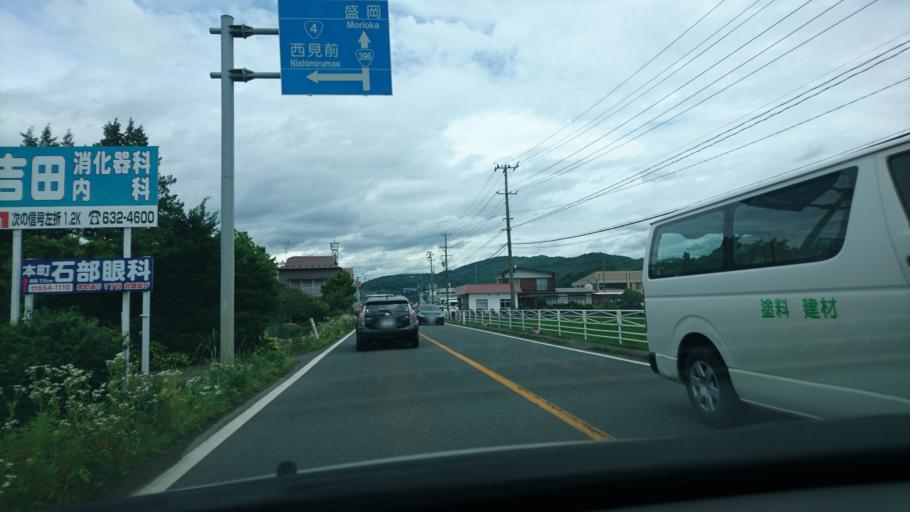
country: JP
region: Iwate
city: Morioka-shi
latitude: 39.6418
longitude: 141.1855
